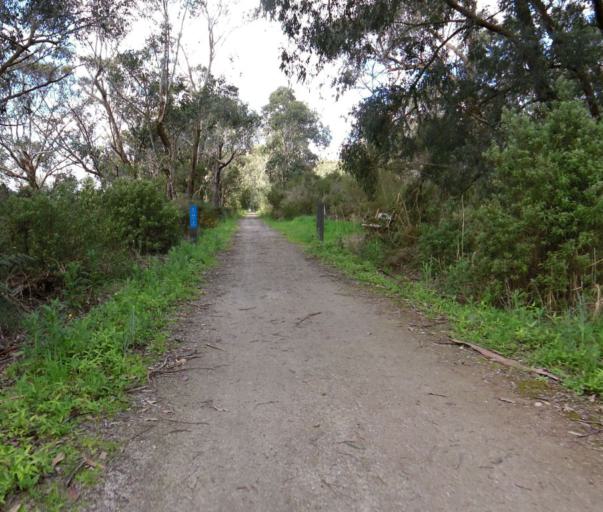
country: AU
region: Victoria
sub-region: Bass Coast
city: North Wonthaggi
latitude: -38.5803
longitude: 146.0325
